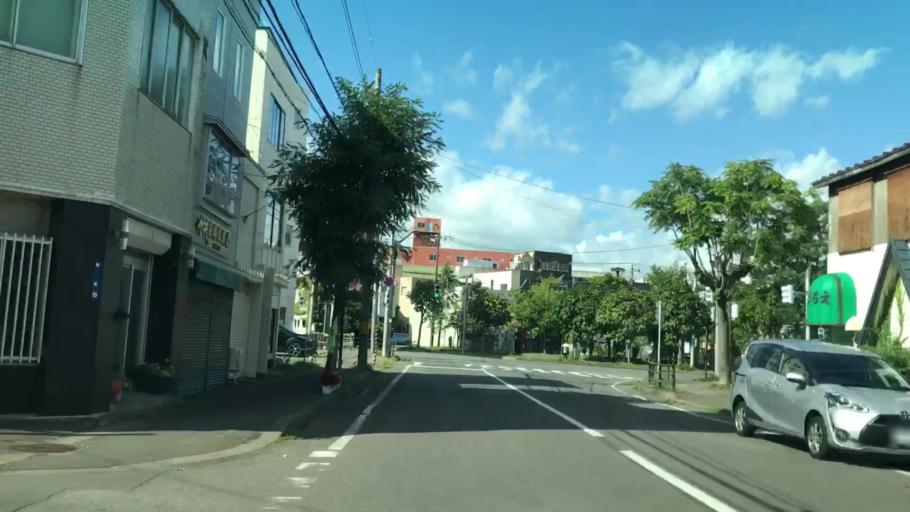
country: JP
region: Hokkaido
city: Muroran
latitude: 42.3158
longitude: 140.9720
